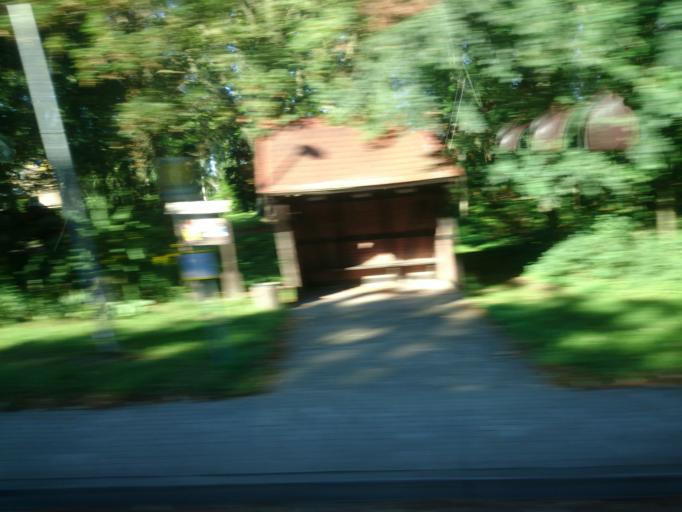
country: DE
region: Mecklenburg-Vorpommern
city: Anklam
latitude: 53.8867
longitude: 13.6766
